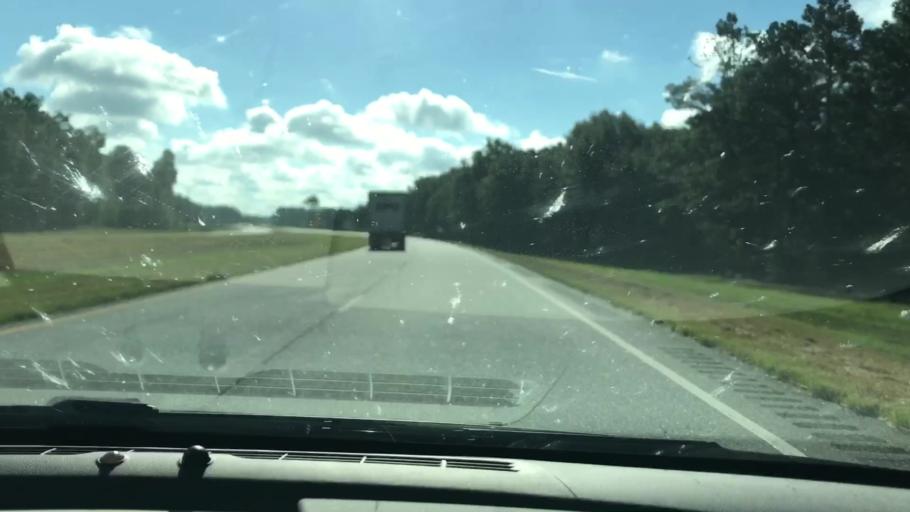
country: US
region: Georgia
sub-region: Dougherty County
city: Putney
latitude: 31.5574
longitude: -84.0057
